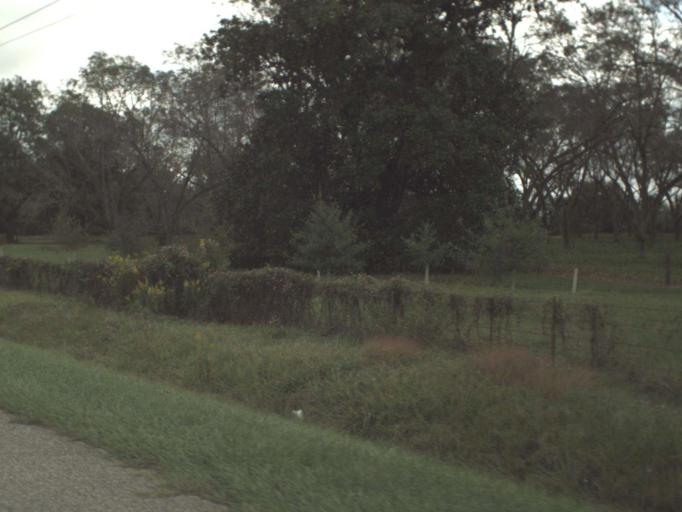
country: US
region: Florida
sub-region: Calhoun County
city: Blountstown
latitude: 30.5443
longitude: -85.1299
